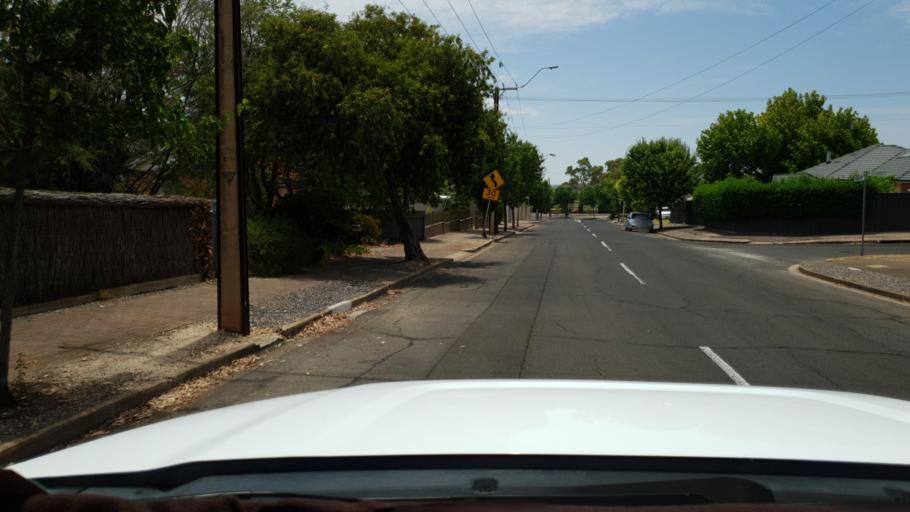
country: AU
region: South Australia
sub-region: Marion
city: Clovelly Park
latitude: -35.0051
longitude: 138.5846
